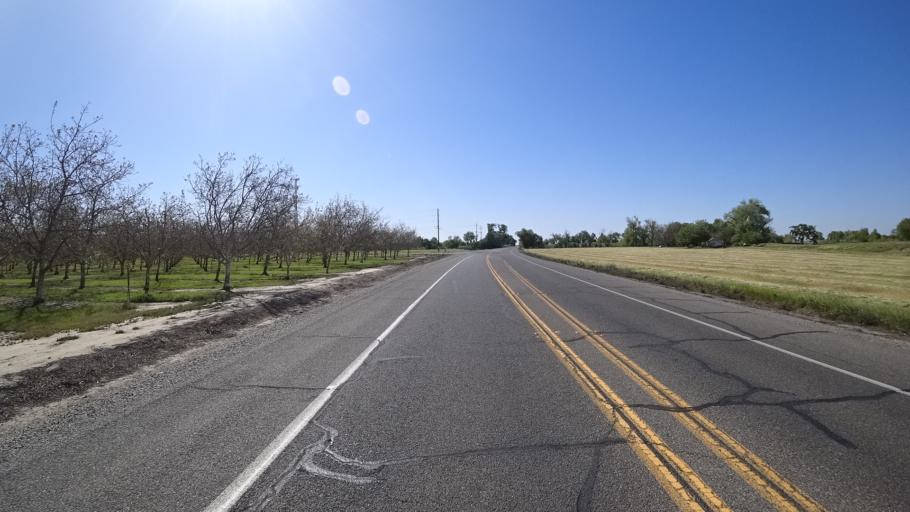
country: US
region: California
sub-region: Glenn County
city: Hamilton City
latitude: 39.7139
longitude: -122.0055
